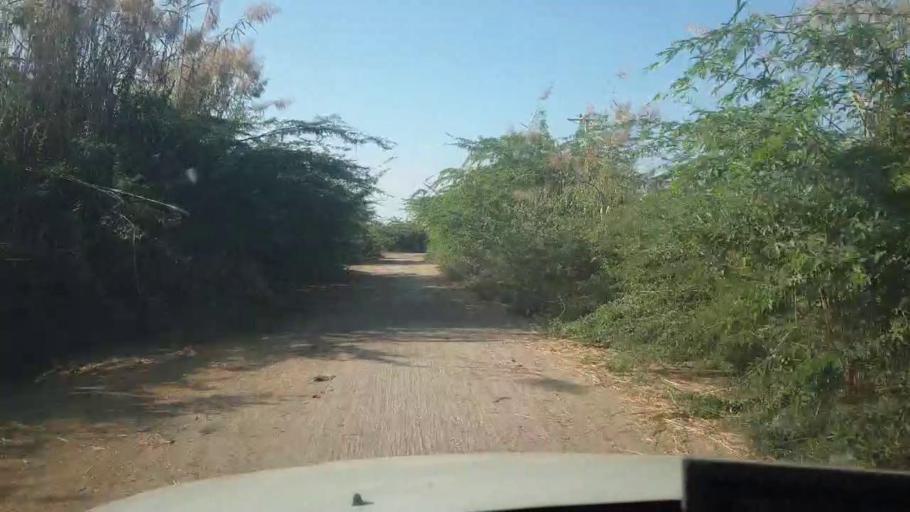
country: PK
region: Sindh
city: Mirpur Sakro
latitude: 24.4883
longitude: 67.6331
